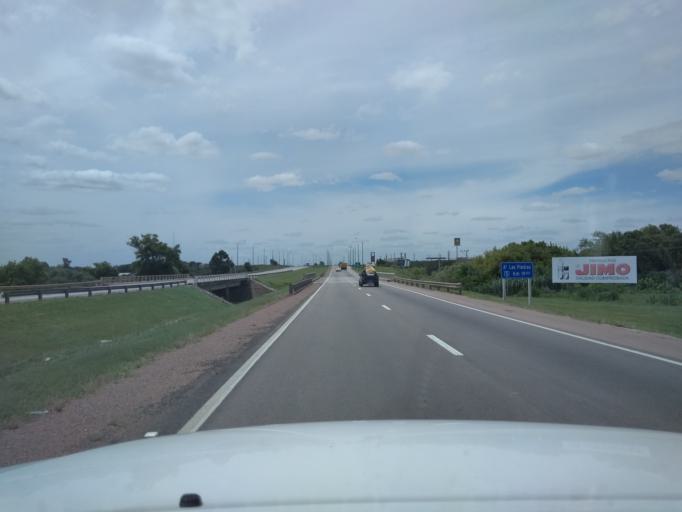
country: UY
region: Canelones
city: La Paz
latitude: -34.7547
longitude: -56.2580
